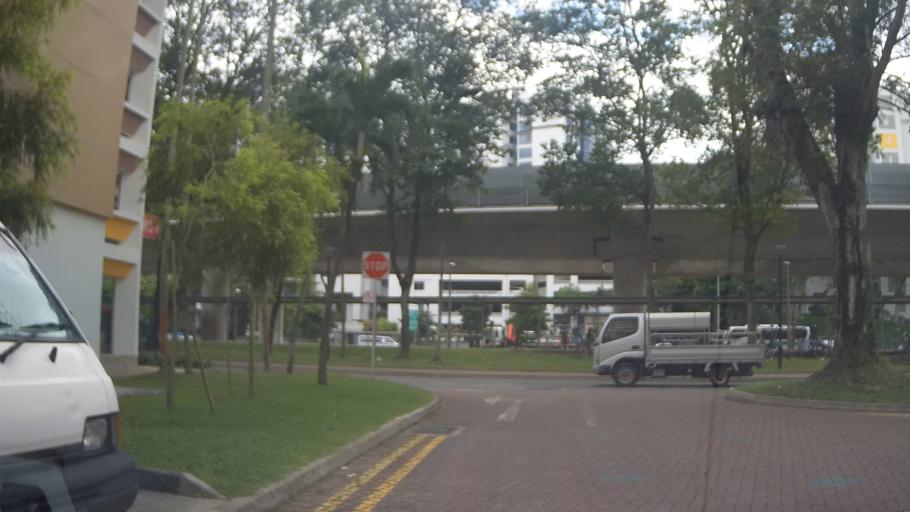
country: MY
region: Johor
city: Johor Bahru
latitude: 1.3993
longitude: 103.7474
